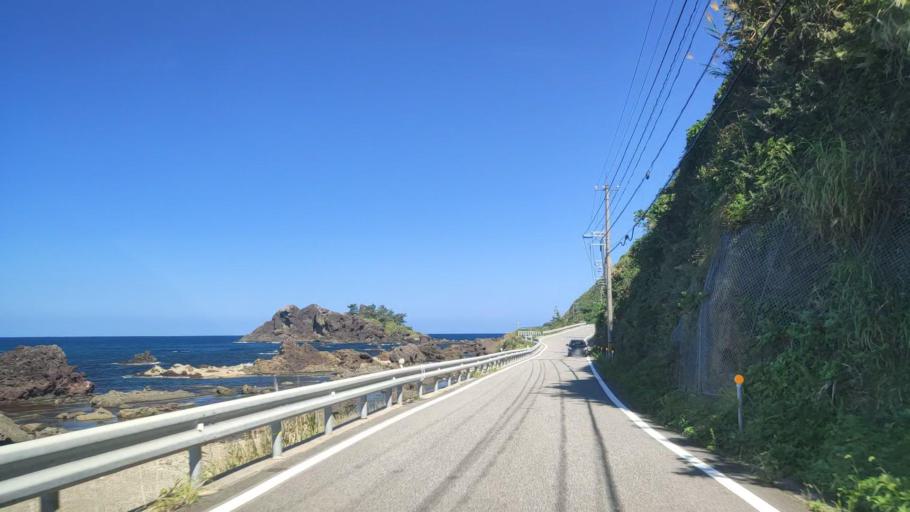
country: JP
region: Ishikawa
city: Nanao
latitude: 37.5051
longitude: 137.1978
